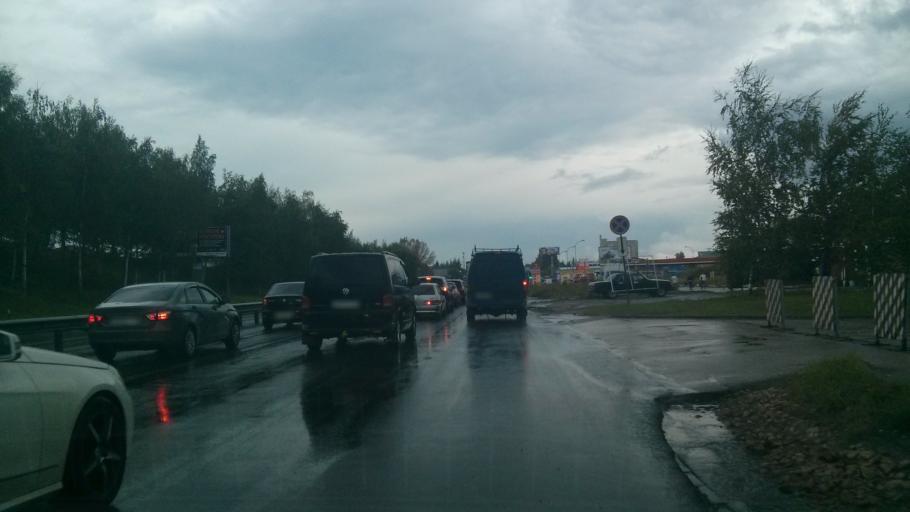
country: RU
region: Nizjnij Novgorod
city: Afonino
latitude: 56.2371
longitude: 44.0122
